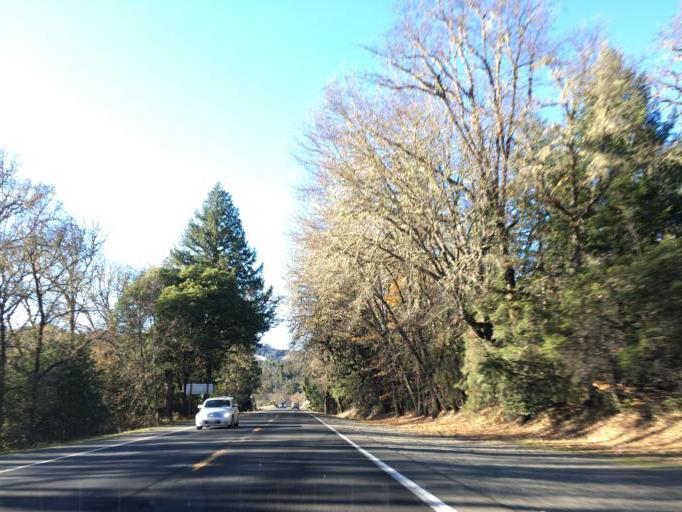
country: US
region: California
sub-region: Mendocino County
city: Laytonville
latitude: 39.7481
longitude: -123.5281
